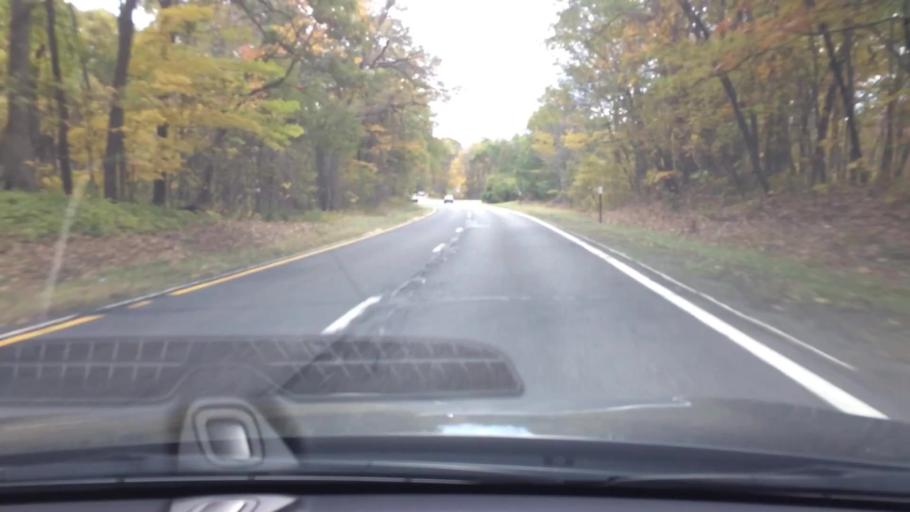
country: US
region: New York
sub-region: Dutchess County
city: Pleasant Valley
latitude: 41.7161
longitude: -73.7841
